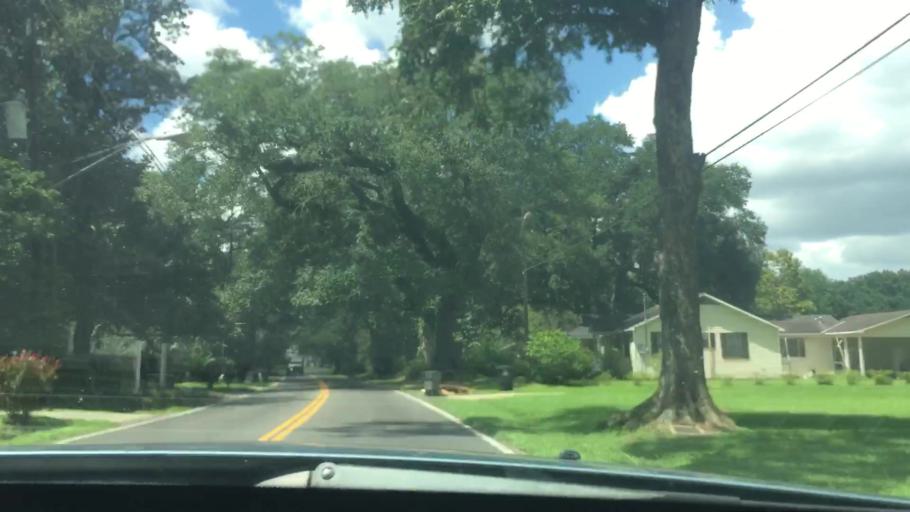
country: US
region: Louisiana
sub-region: East Baton Rouge Parish
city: Gardere
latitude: 30.3720
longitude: -91.1279
